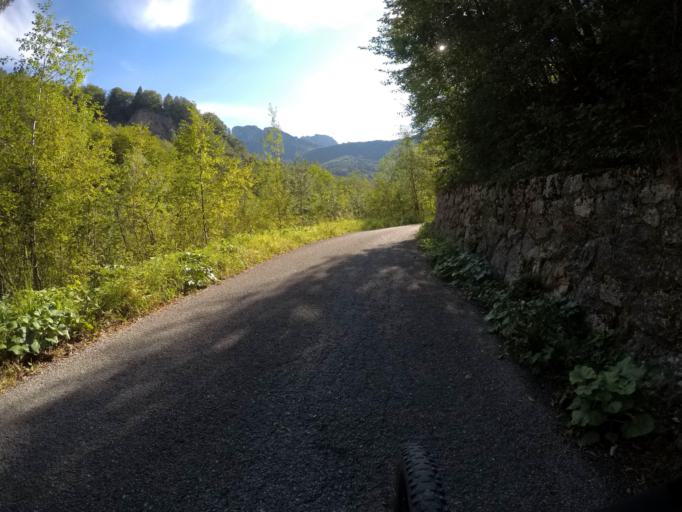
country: IT
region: Friuli Venezia Giulia
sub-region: Provincia di Udine
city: Zuglio
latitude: 46.4360
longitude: 13.0752
